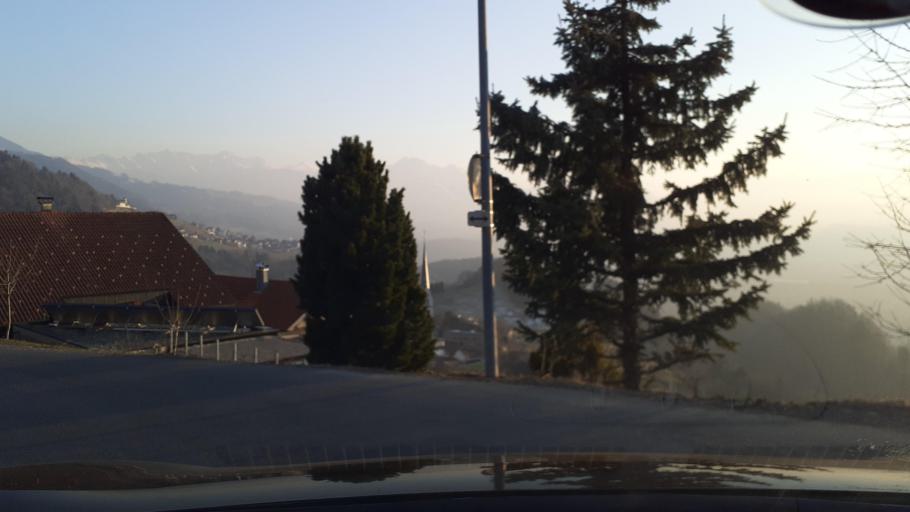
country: AT
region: Vorarlberg
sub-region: Politischer Bezirk Feldkirch
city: Fraxern
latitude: 47.3182
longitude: 9.6743
